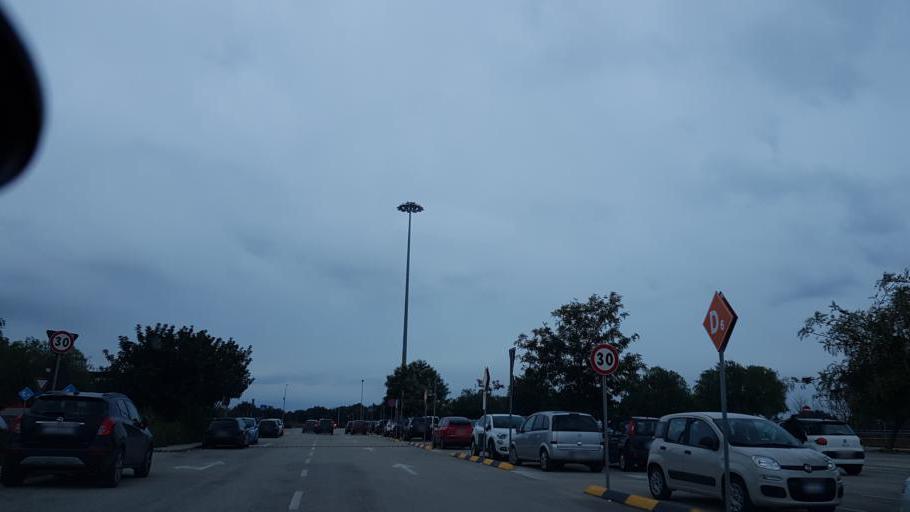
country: IT
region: Apulia
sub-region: Provincia di Brindisi
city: Mesagne
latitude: 40.5787
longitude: 17.8376
